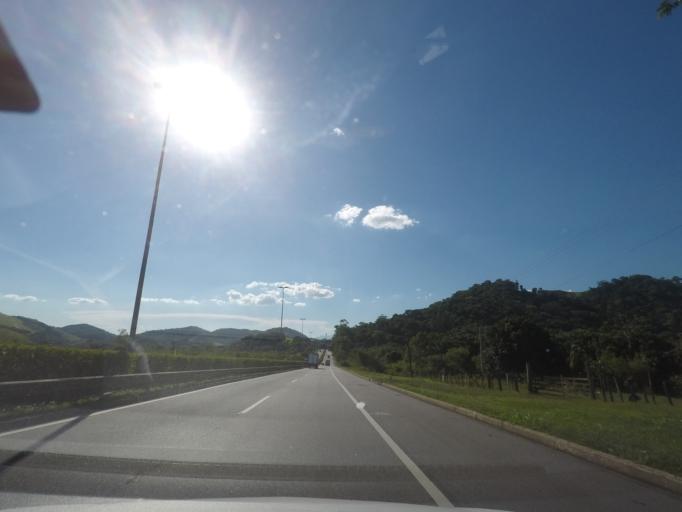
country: BR
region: Rio de Janeiro
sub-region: Sao Goncalo
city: Sao Goncalo
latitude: -22.6653
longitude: -43.1068
